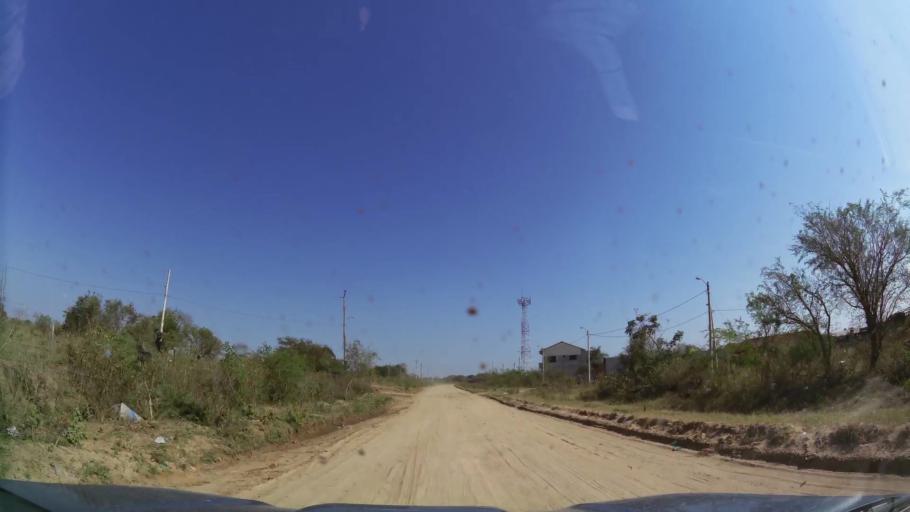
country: BO
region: Santa Cruz
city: Cotoca
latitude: -17.7264
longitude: -63.0704
